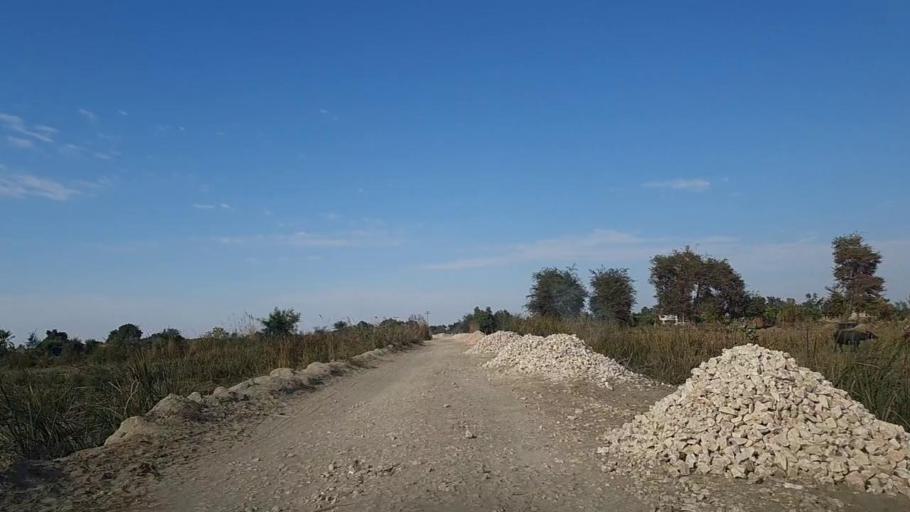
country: PK
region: Sindh
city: Khadro
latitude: 26.3042
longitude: 68.8141
